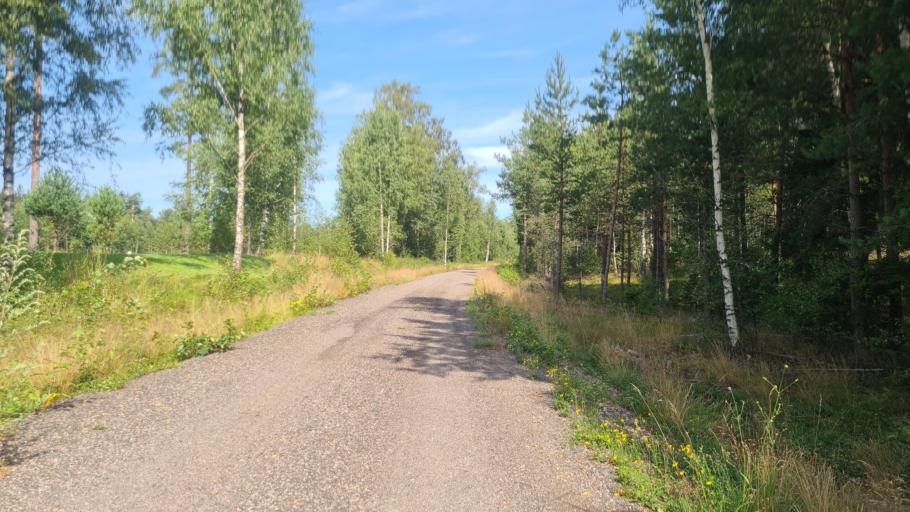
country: SE
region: Kronoberg
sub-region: Ljungby Kommun
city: Lagan
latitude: 56.9294
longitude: 13.9792
